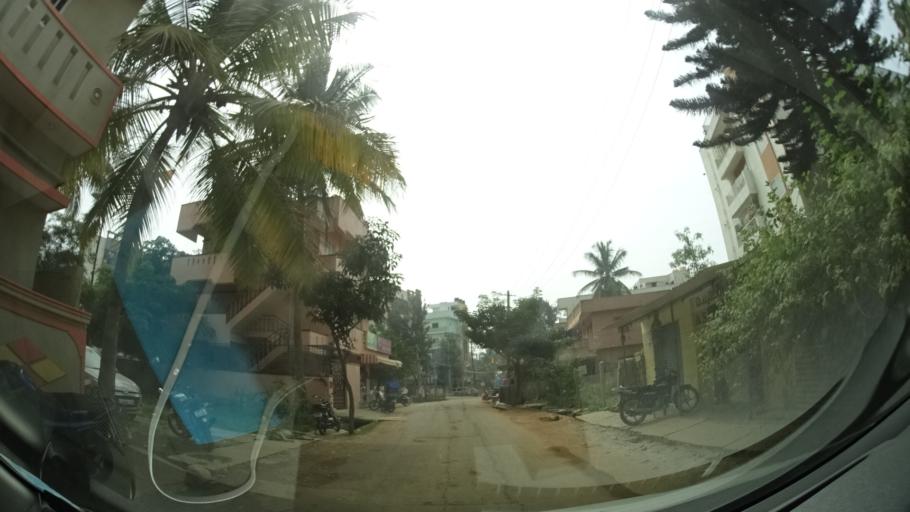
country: IN
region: Karnataka
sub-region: Bangalore Rural
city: Hoskote
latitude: 12.9661
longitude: 77.7565
